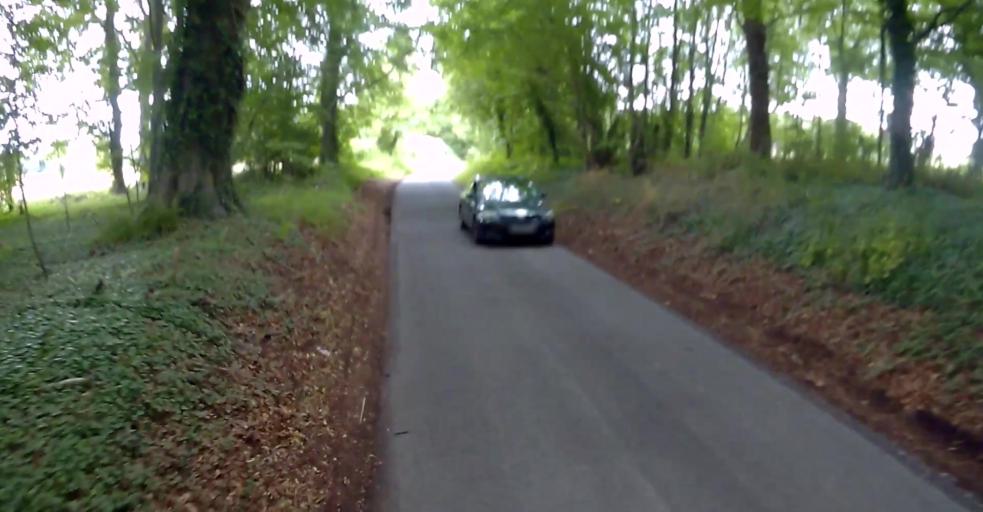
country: GB
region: England
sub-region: Hampshire
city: Kings Worthy
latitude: 51.0761
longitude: -1.2039
